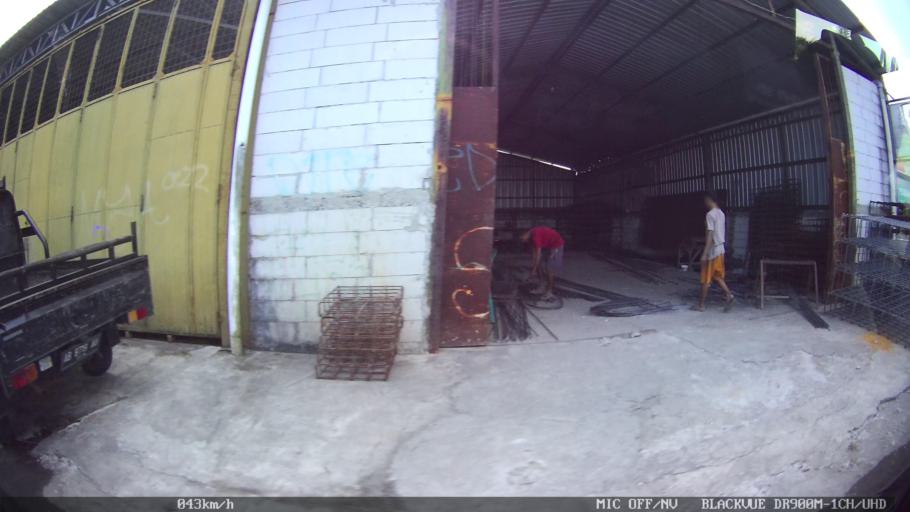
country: ID
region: Daerah Istimewa Yogyakarta
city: Bantul
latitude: -7.9073
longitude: 110.3431
